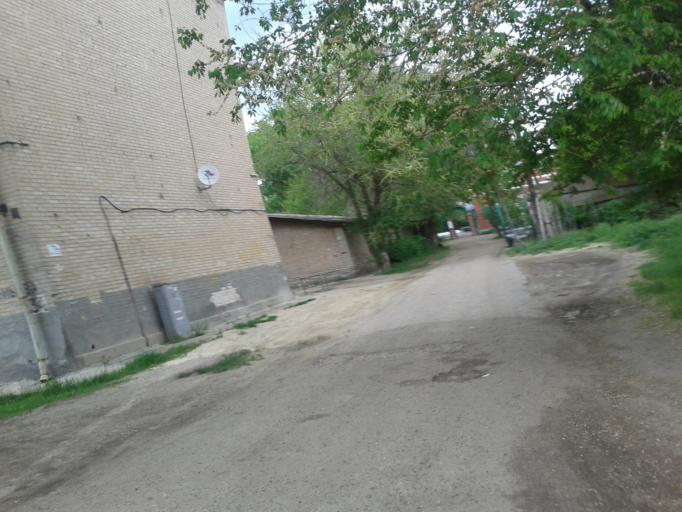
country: RU
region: Volgograd
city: Krasnoslobodsk
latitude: 48.5211
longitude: 44.5112
